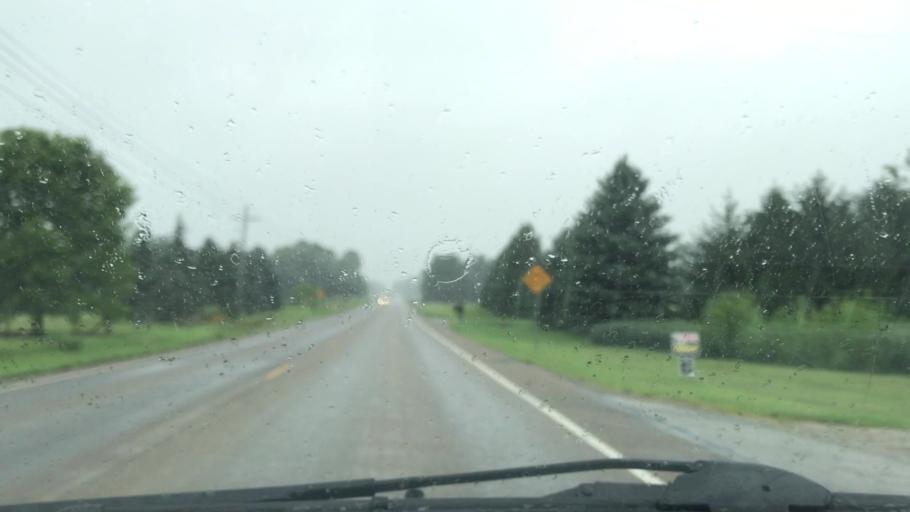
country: US
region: Indiana
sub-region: Hamilton County
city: Sheridan
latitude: 40.1219
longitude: -86.1913
